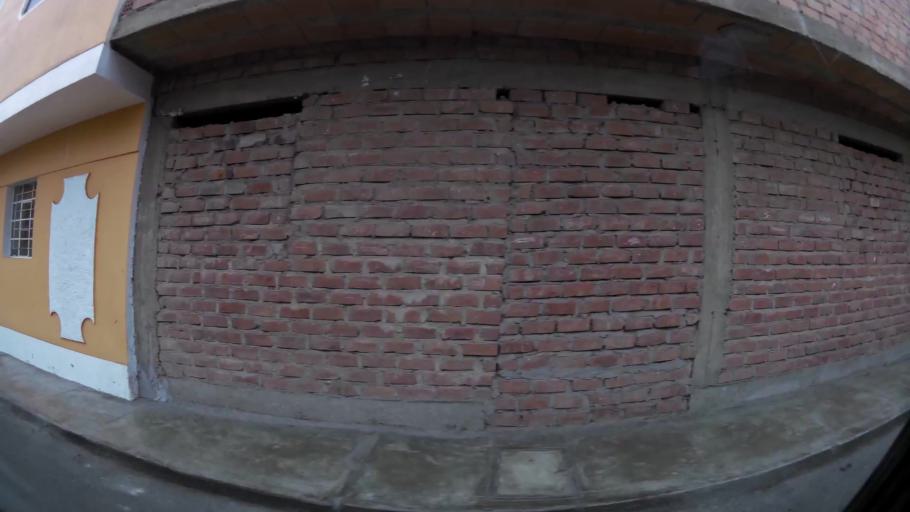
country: PE
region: Lima
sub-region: Barranca
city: Barranca
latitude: -10.7478
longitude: -77.7568
